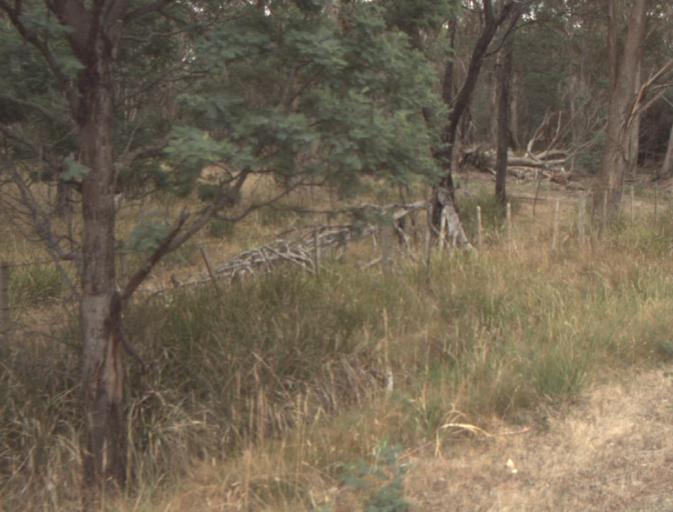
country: AU
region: Tasmania
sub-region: Northern Midlands
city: Evandale
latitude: -41.5121
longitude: 147.3403
